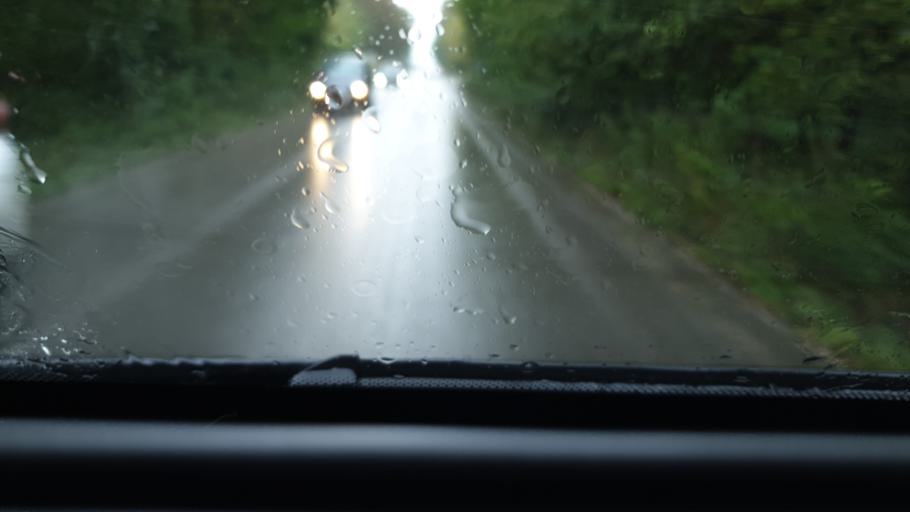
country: BE
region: Wallonia
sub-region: Province du Hainaut
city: Chatelet
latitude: 50.3826
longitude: 4.4859
